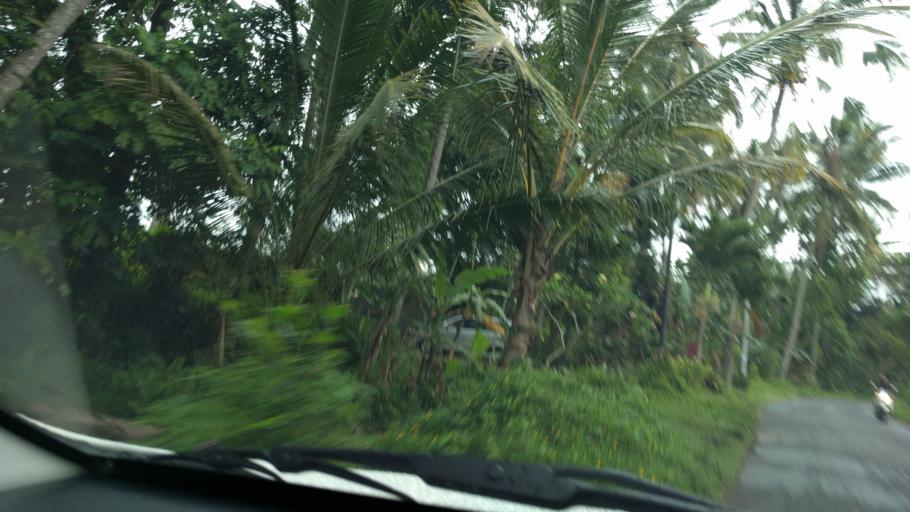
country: ID
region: Bali
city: Banjar Triwangsakeliki
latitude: -8.4578
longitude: 115.2599
